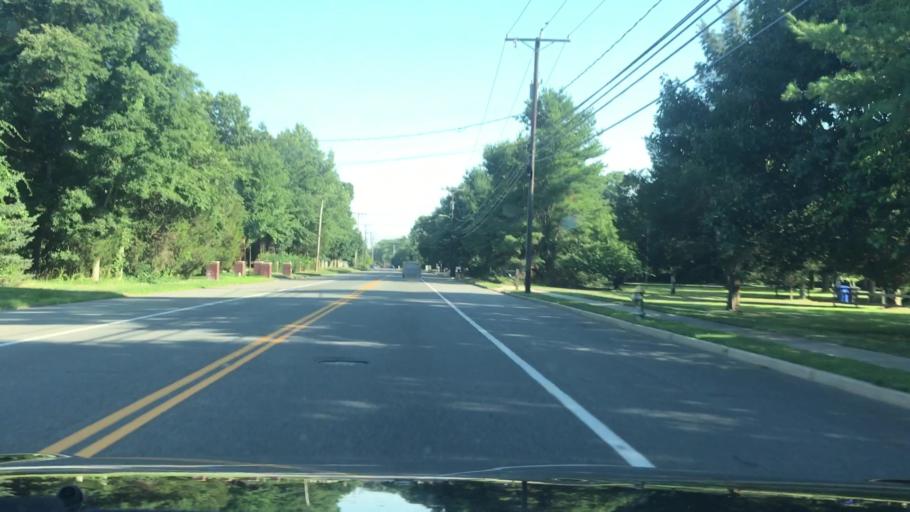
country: US
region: New Jersey
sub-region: Ocean County
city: Leisure Village
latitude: 40.0247
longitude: -74.2006
